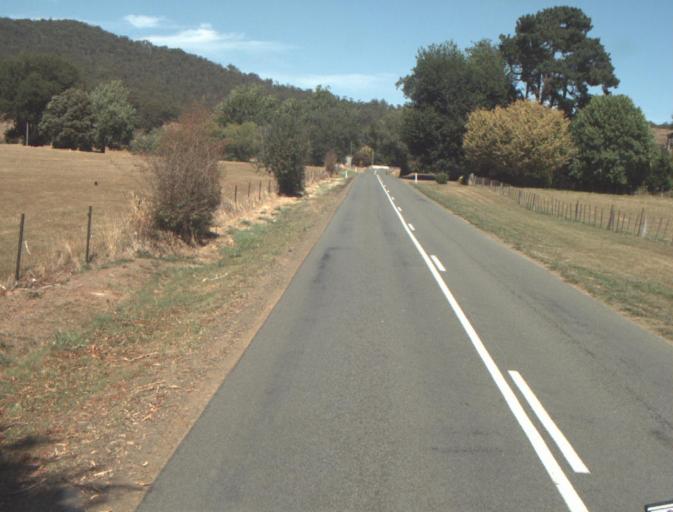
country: AU
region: Tasmania
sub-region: Launceston
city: Mayfield
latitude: -41.2623
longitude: 147.1353
